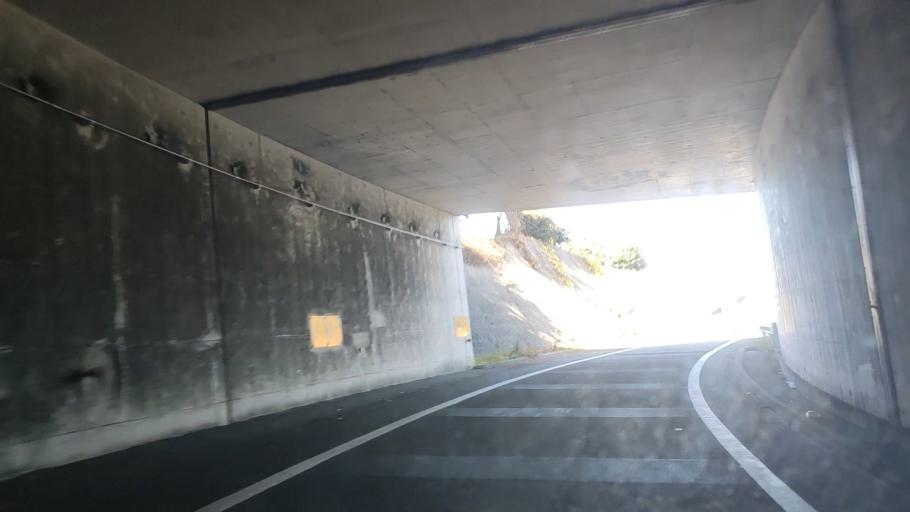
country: JP
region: Ehime
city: Saijo
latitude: 33.9120
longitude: 133.2368
